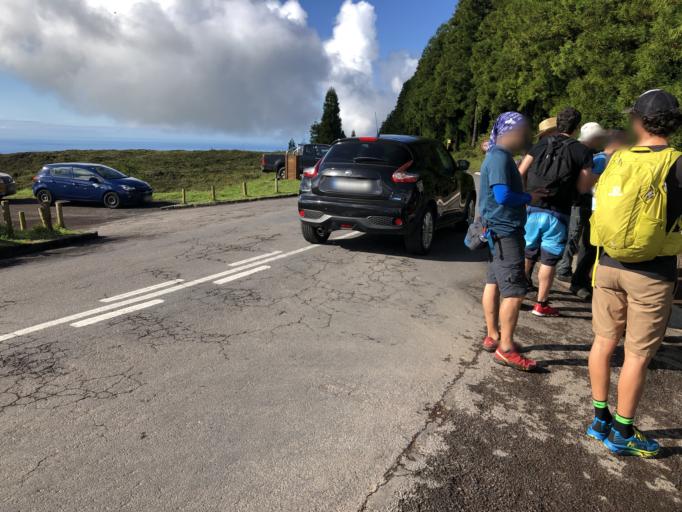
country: PT
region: Azores
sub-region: Ponta Delgada
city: Arrifes
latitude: 37.8350
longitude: -25.7586
